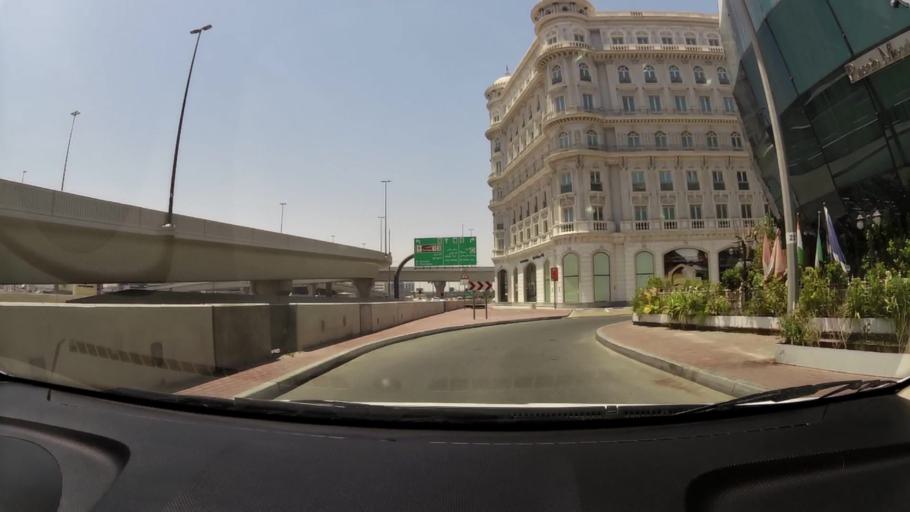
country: AE
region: Ash Shariqah
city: Sharjah
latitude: 25.2574
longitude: 55.3368
